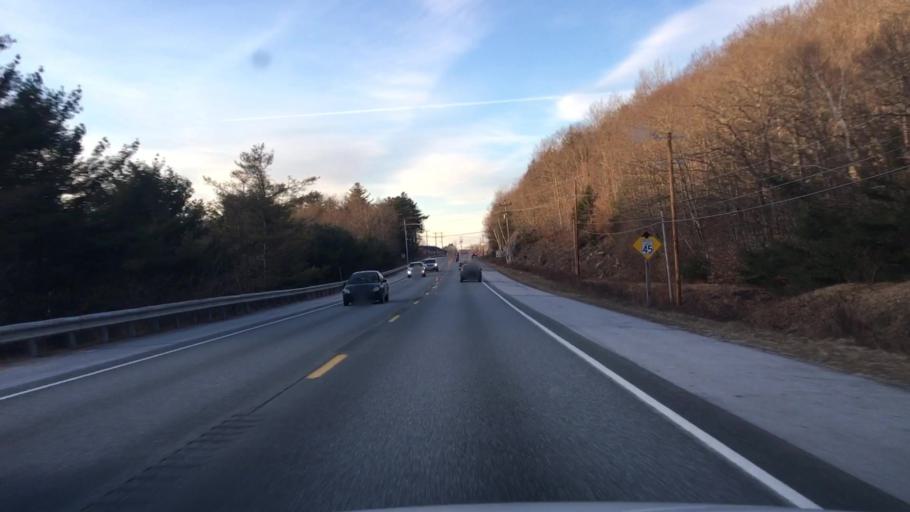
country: US
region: Maine
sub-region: Hancock County
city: Dedham
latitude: 44.7238
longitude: -68.6187
